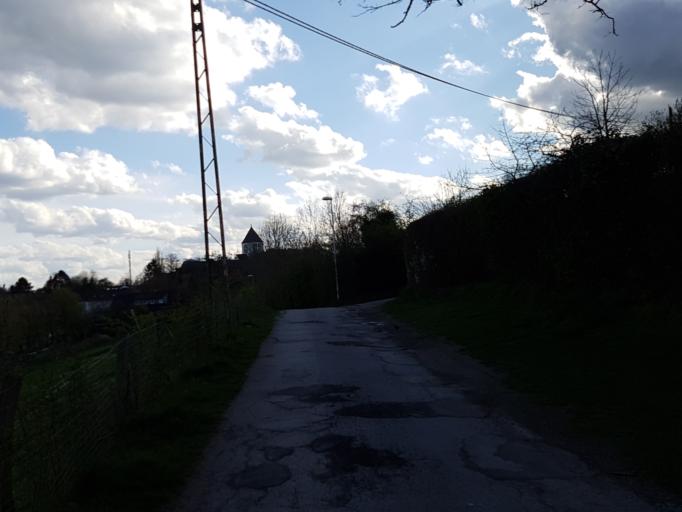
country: DE
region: North Rhine-Westphalia
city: Stolberg
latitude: 50.7334
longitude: 6.1713
